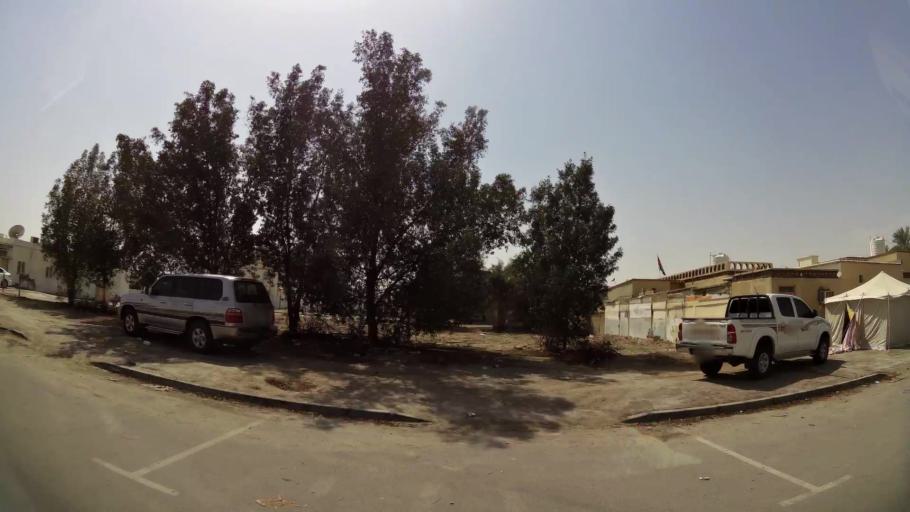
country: AE
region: Abu Dhabi
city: Abu Dhabi
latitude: 24.2908
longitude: 54.6462
